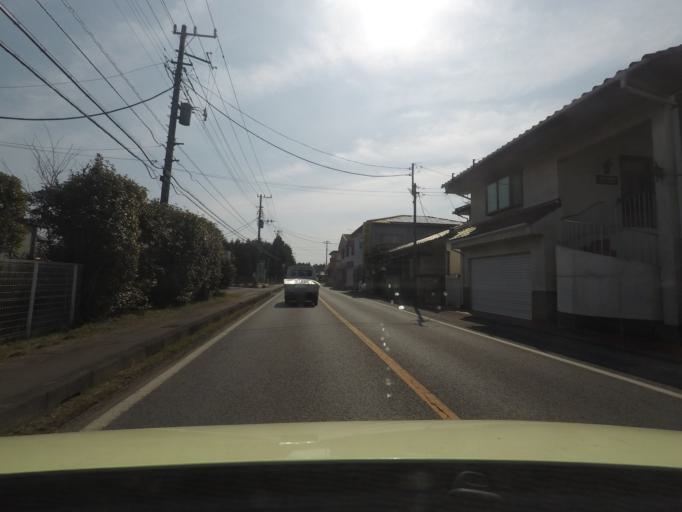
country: JP
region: Ibaraki
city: Naka
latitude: 36.0738
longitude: 140.1500
